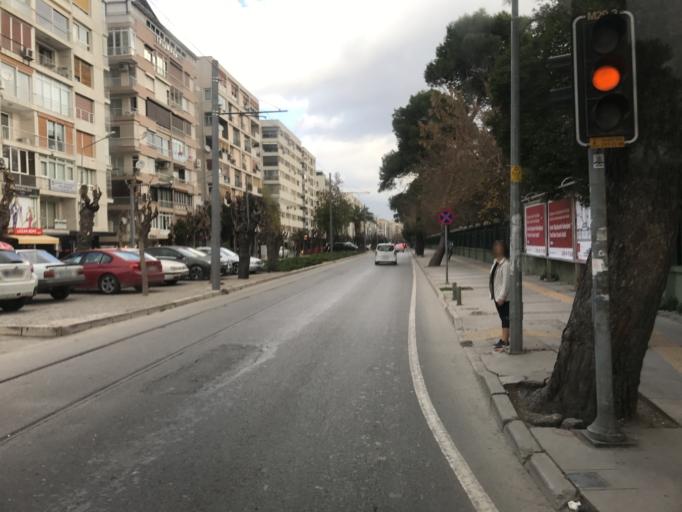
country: TR
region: Izmir
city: Izmir
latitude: 38.4299
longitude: 27.1419
